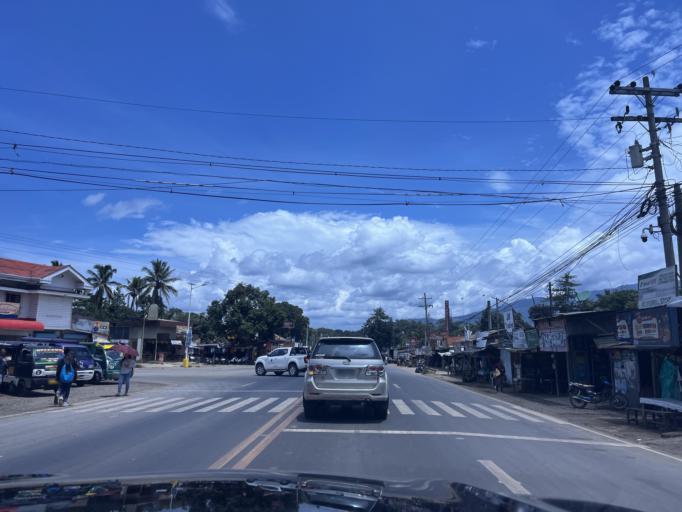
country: PH
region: Northern Mindanao
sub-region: Province of Bukidnon
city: Kisolon
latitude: 8.3274
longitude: 124.9783
